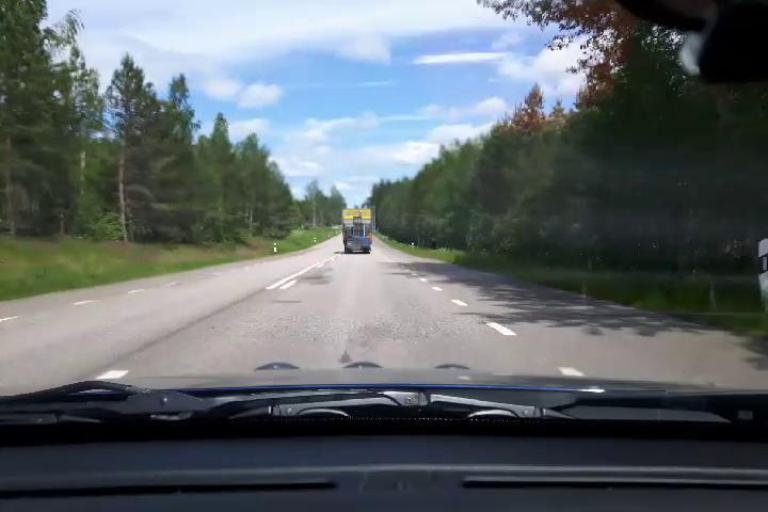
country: SE
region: Uppsala
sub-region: Osthammars Kommun
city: Bjorklinge
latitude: 60.0817
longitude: 17.5452
